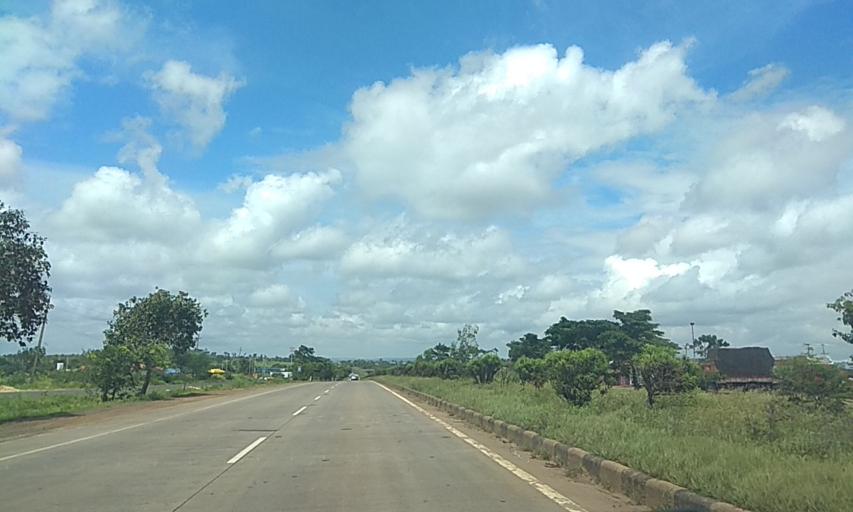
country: IN
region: Karnataka
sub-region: Belgaum
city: Sankeshwar
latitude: 16.1512
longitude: 74.5175
